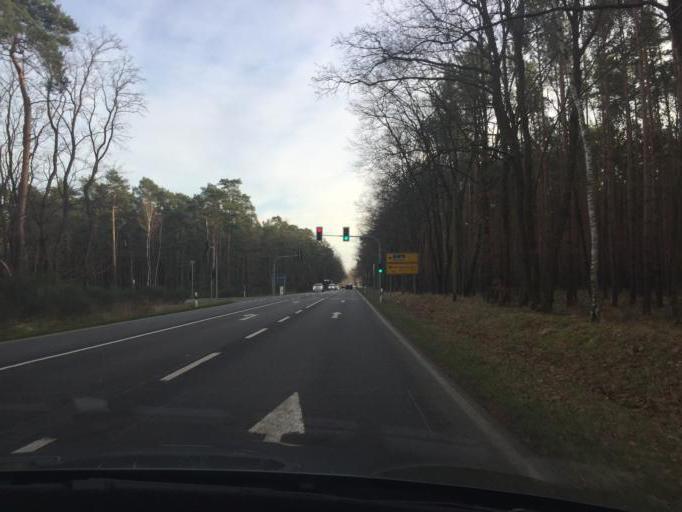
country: DE
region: Brandenburg
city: Cottbus
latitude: 51.7399
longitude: 14.4004
